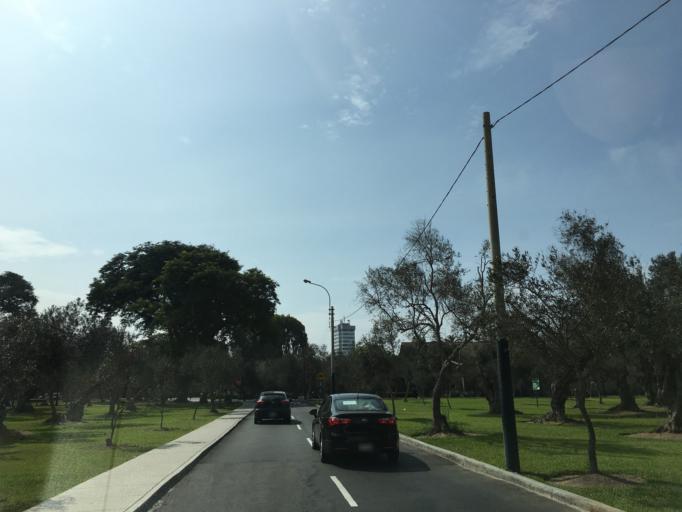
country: PE
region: Lima
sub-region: Lima
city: San Isidro
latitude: -12.1031
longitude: -77.0359
